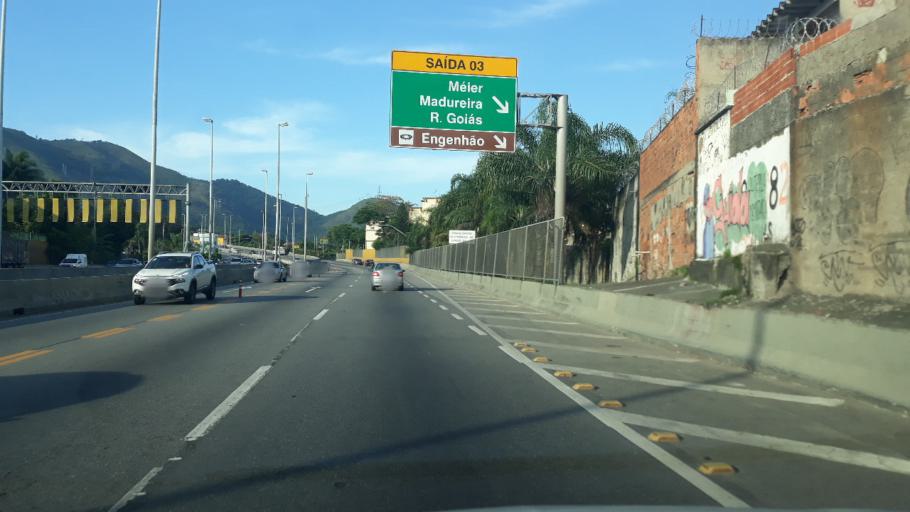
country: BR
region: Rio de Janeiro
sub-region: Rio De Janeiro
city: Rio de Janeiro
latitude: -22.8910
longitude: -43.2978
